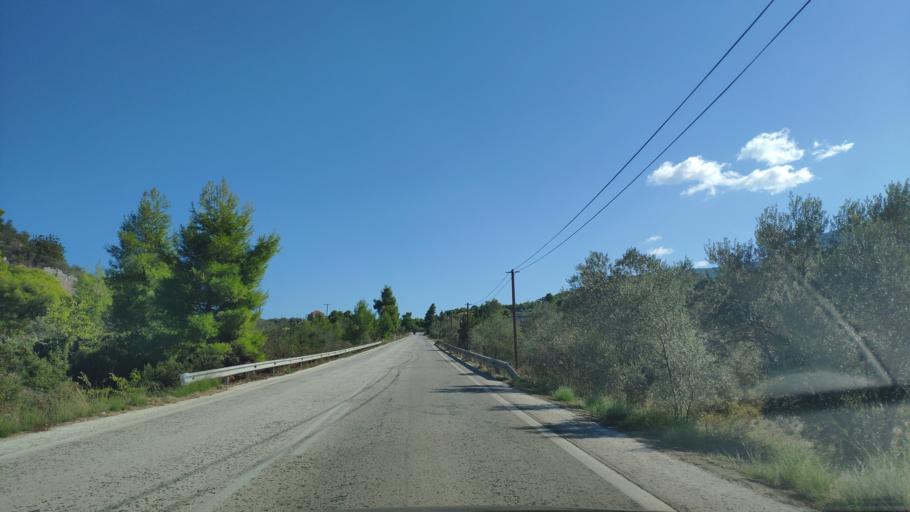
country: GR
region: Peloponnese
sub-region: Nomos Korinthias
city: Loutra Oraias Elenis
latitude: 37.8369
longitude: 23.0071
